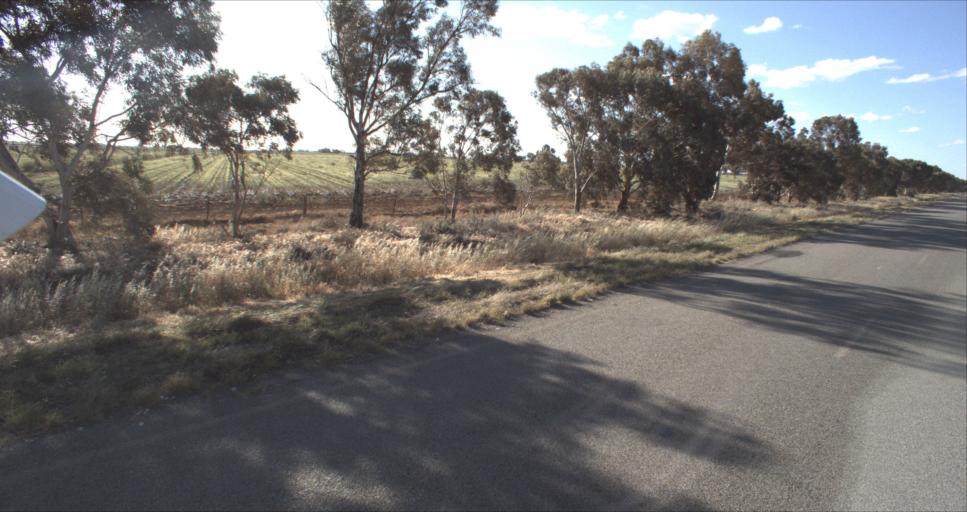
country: AU
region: New South Wales
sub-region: Leeton
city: Leeton
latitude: -34.5519
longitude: 146.2790
